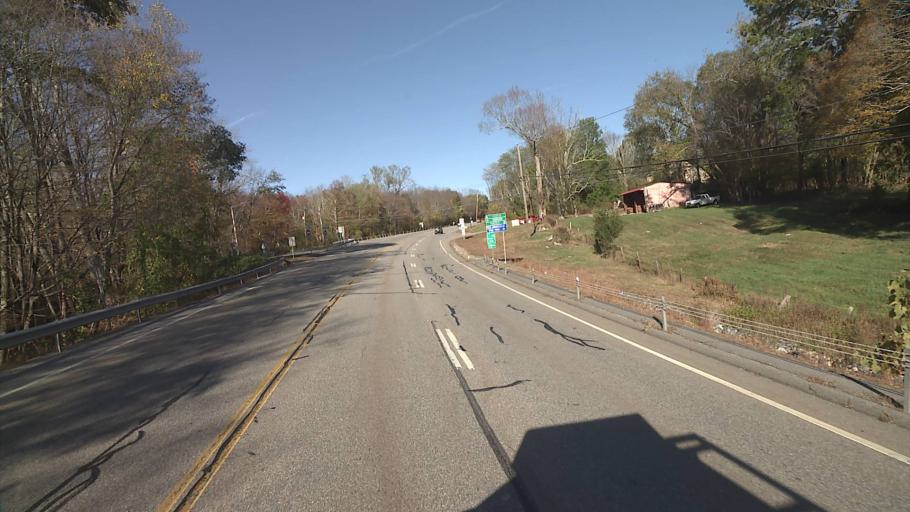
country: US
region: Connecticut
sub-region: Windham County
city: Windham
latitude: 41.7671
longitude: -72.0564
